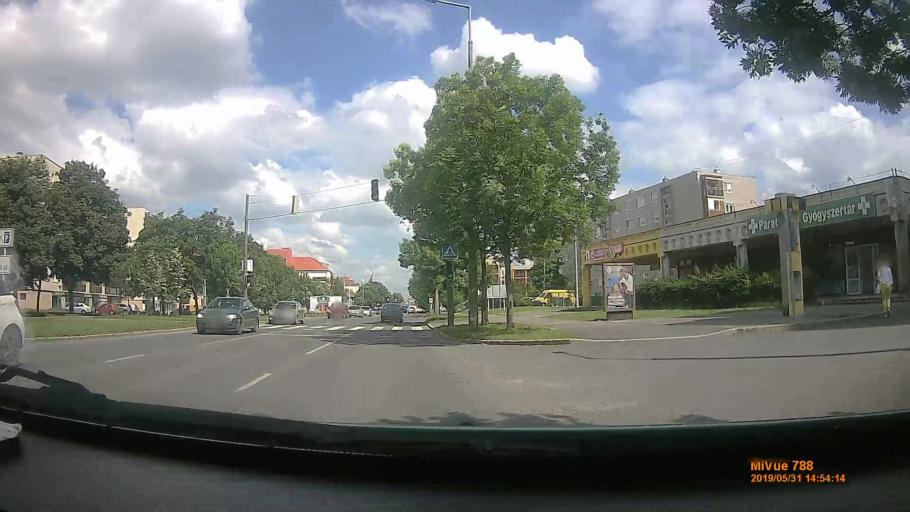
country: HU
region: Borsod-Abauj-Zemplen
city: Miskolc
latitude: 48.0998
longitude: 20.7945
